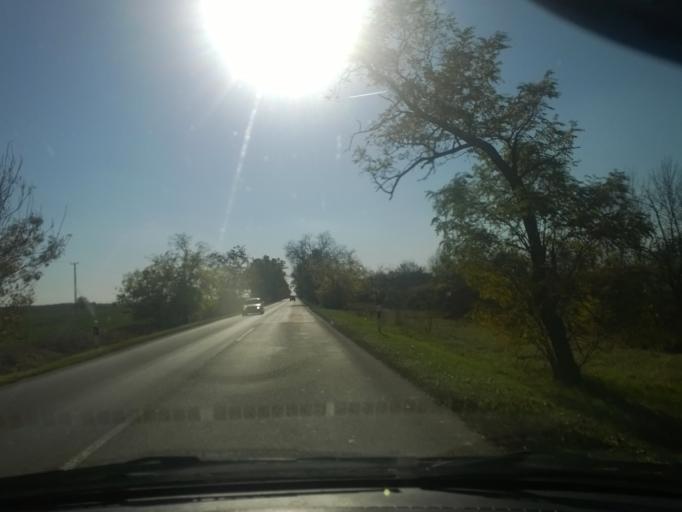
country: HU
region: Csongrad
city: Szegvar
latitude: 46.5531
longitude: 20.3163
